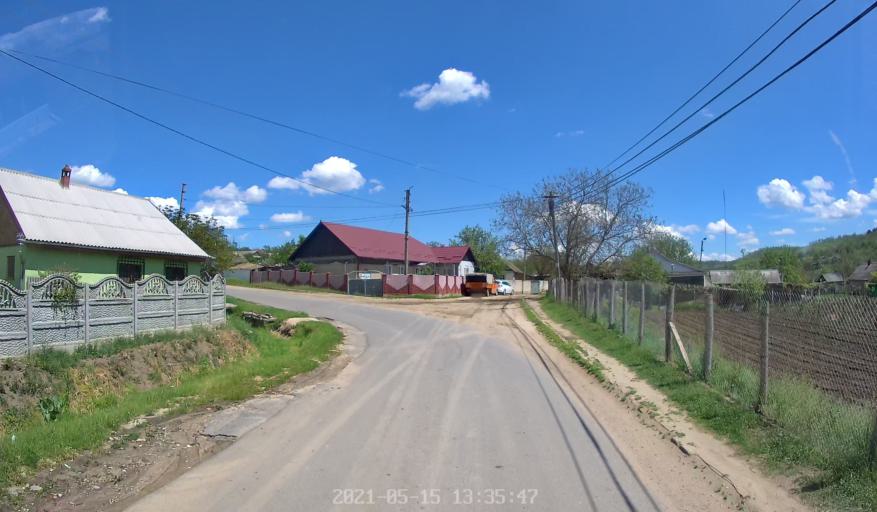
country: NG
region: Niger
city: Kutigi
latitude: 9.3401
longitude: 5.7054
